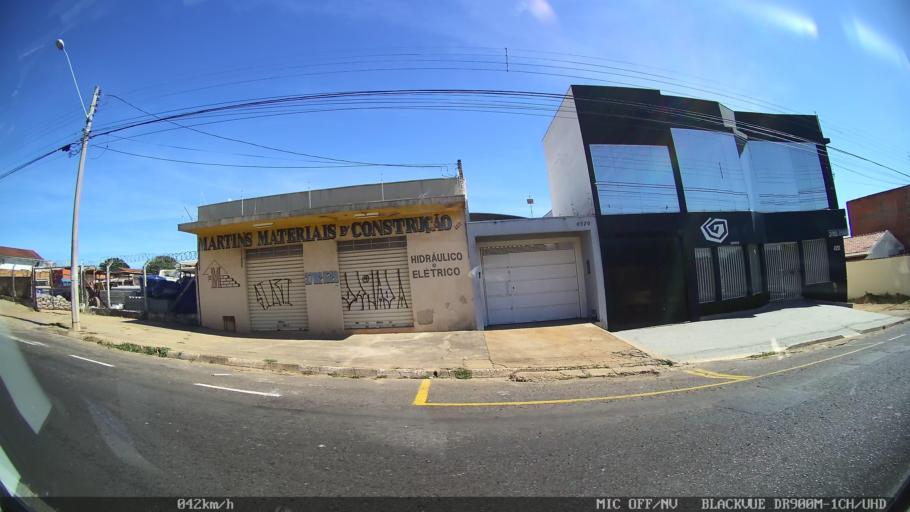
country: BR
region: Sao Paulo
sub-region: Franca
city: Franca
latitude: -20.5557
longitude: -47.3719
